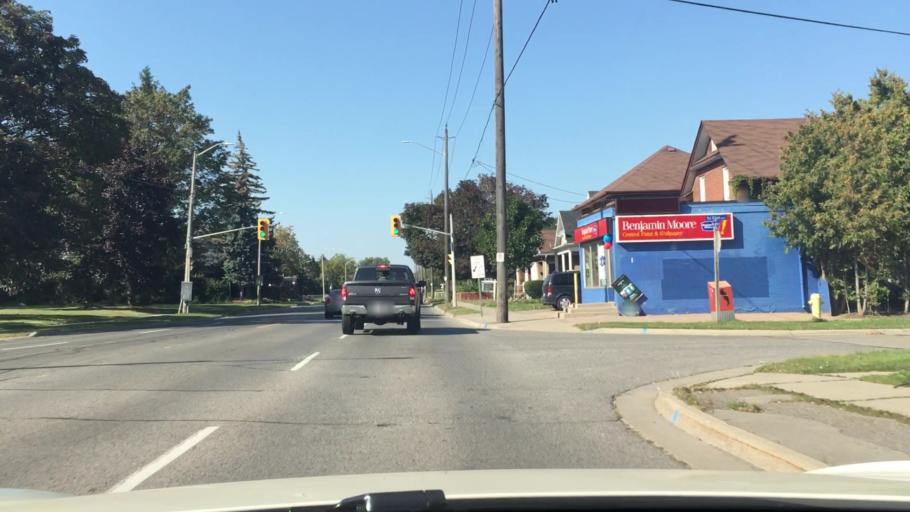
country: CA
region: Ontario
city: Oshawa
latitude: 43.8920
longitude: -78.8502
